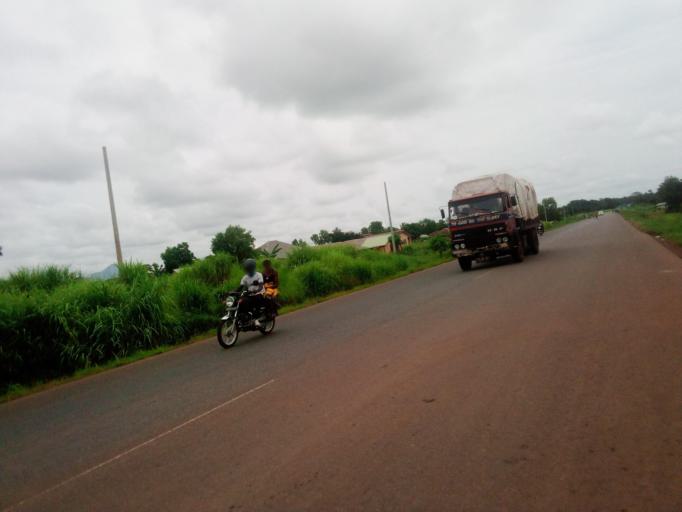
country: SL
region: Northern Province
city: Kambia
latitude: 9.0988
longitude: -12.9171
